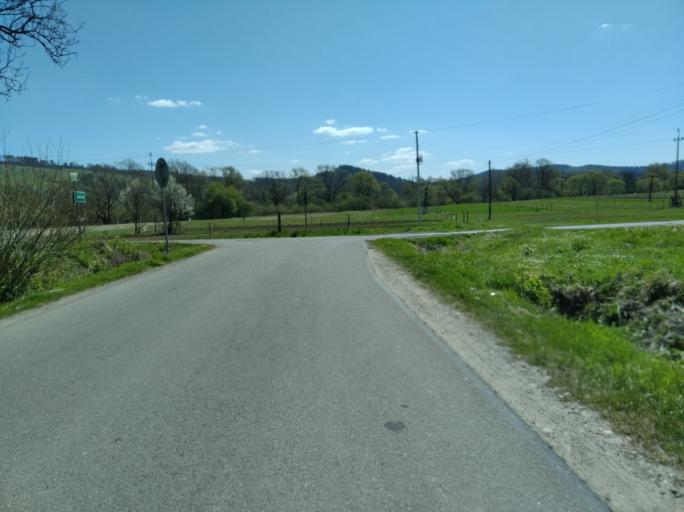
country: PL
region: Subcarpathian Voivodeship
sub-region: Powiat brzozowski
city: Dydnia
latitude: 49.7111
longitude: 22.2004
